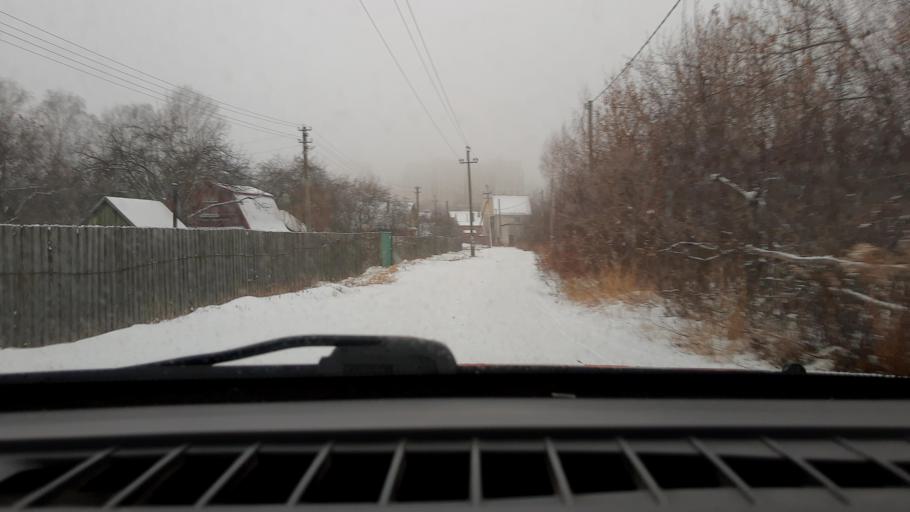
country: RU
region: Nizjnij Novgorod
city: Nizhniy Novgorod
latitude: 56.2374
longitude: 43.9867
